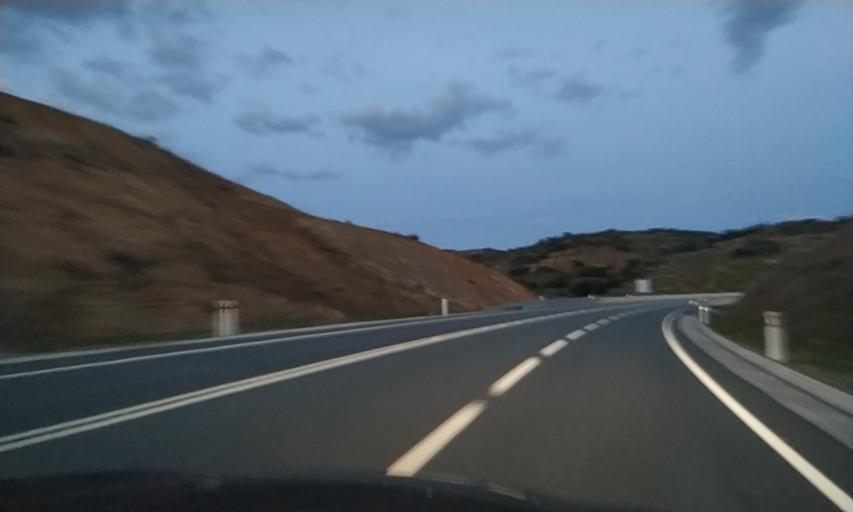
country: PT
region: Braganca
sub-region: Alfandega da Fe
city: Alfandega da Fe
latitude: 41.3083
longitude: -6.9106
